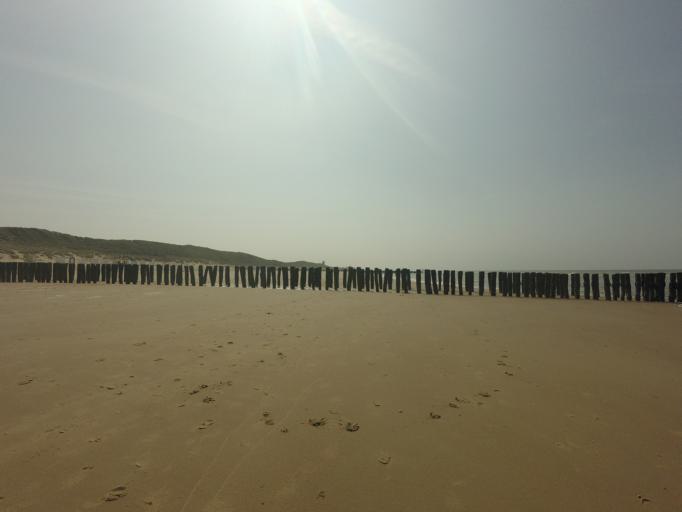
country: NL
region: Zeeland
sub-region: Gemeente Middelburg
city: Middelburg
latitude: 51.5739
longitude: 3.5137
